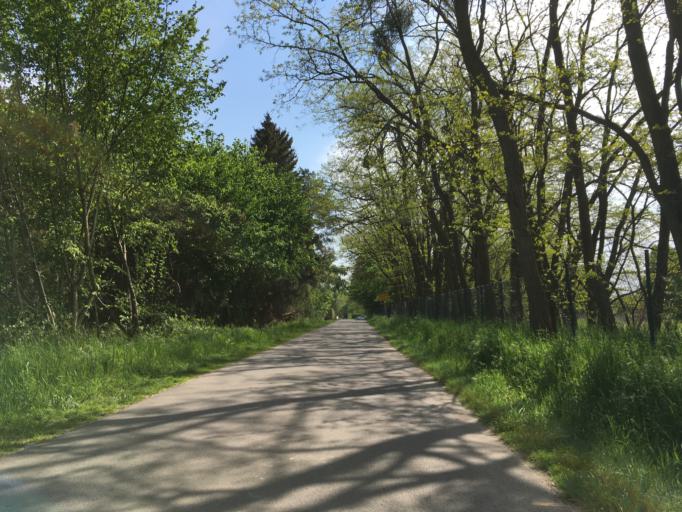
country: DE
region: Brandenburg
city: Werneuchen
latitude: 52.6005
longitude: 13.7431
